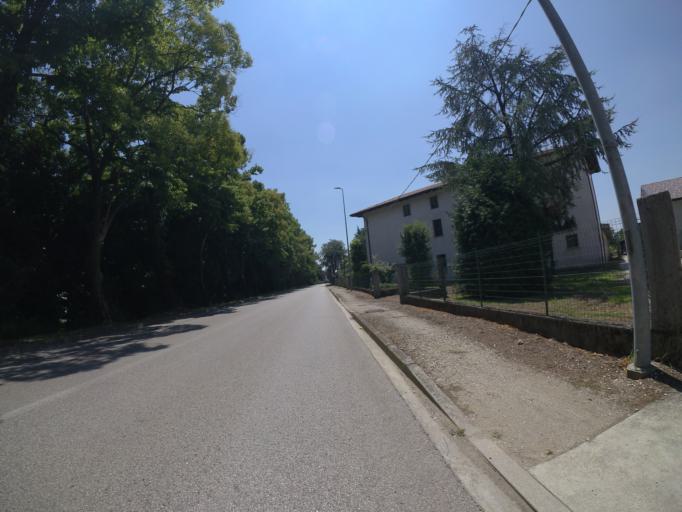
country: IT
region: Friuli Venezia Giulia
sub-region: Provincia di Udine
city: Lestizza
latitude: 45.9753
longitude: 13.1396
